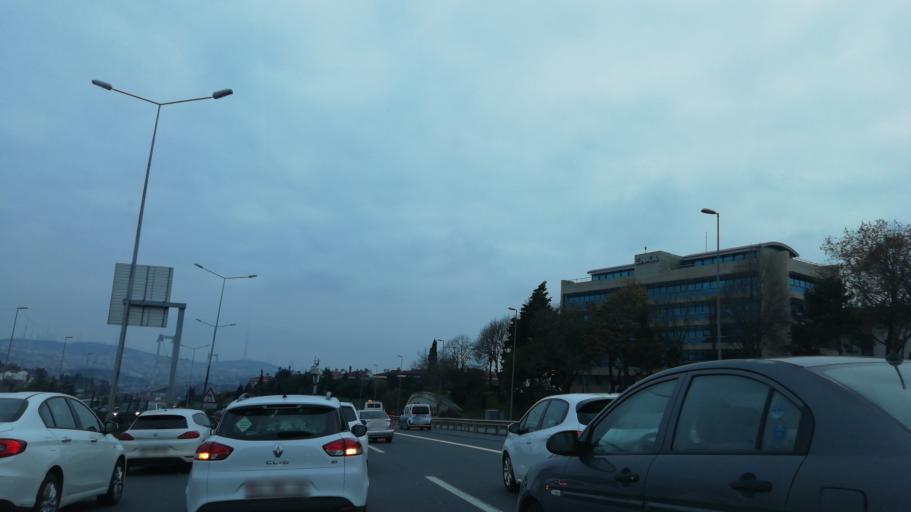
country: TR
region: Istanbul
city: Sisli
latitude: 41.0589
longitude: 29.0170
